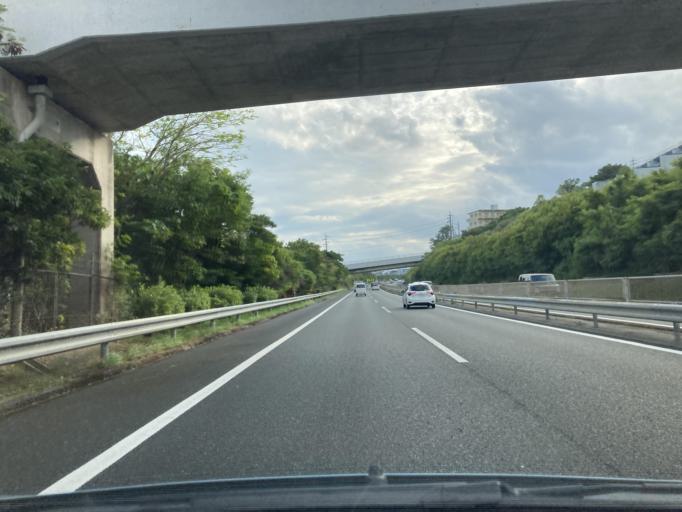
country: JP
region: Okinawa
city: Ginowan
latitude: 26.2665
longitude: 127.7744
